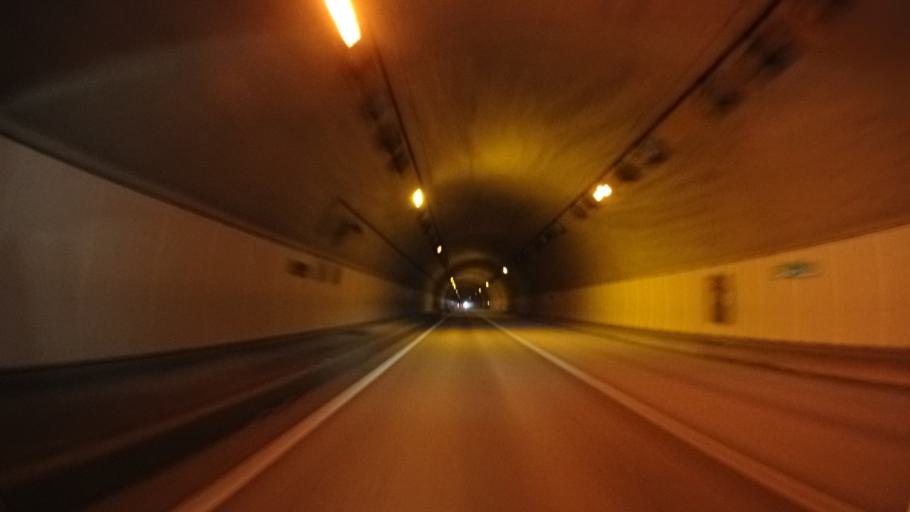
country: JP
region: Ehime
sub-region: Nishiuwa-gun
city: Ikata-cho
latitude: 33.5089
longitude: 132.3961
